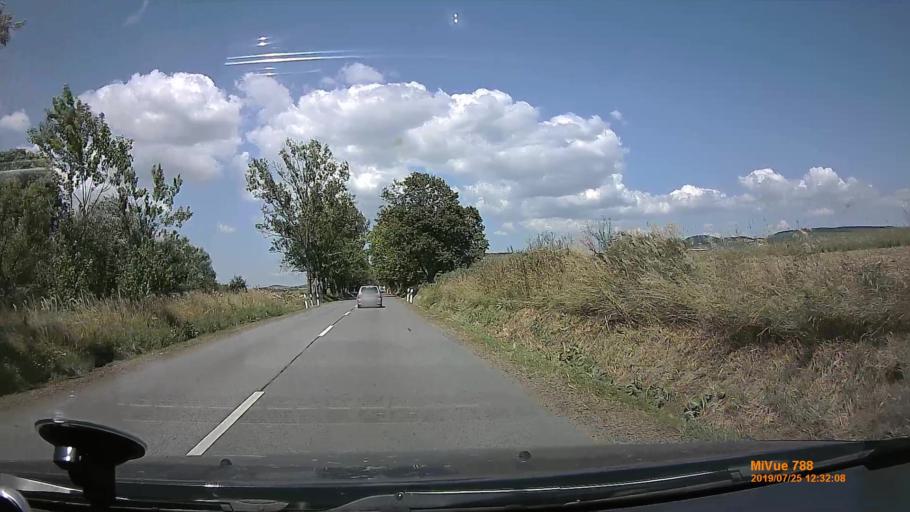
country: HU
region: Borsod-Abauj-Zemplen
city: Tarcal
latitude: 48.1483
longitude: 21.3189
